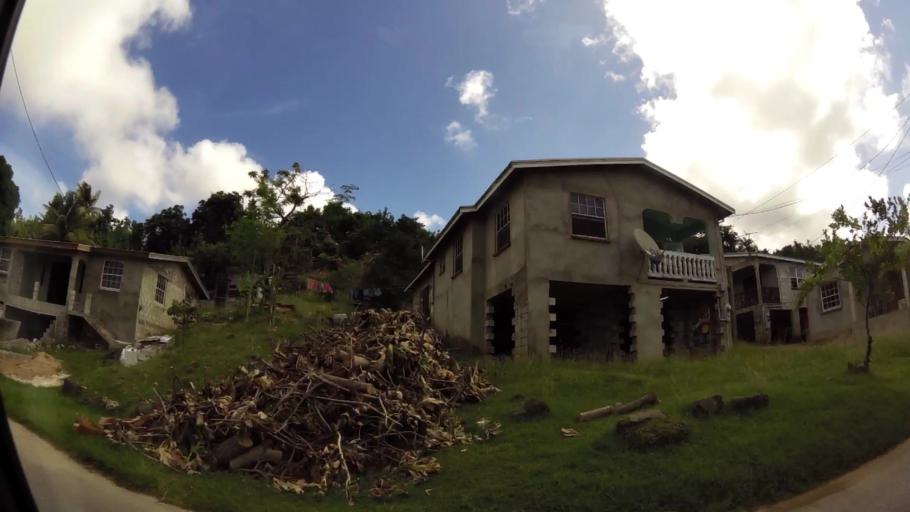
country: BB
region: Saint James
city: Holetown
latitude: 13.2112
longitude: -59.6058
